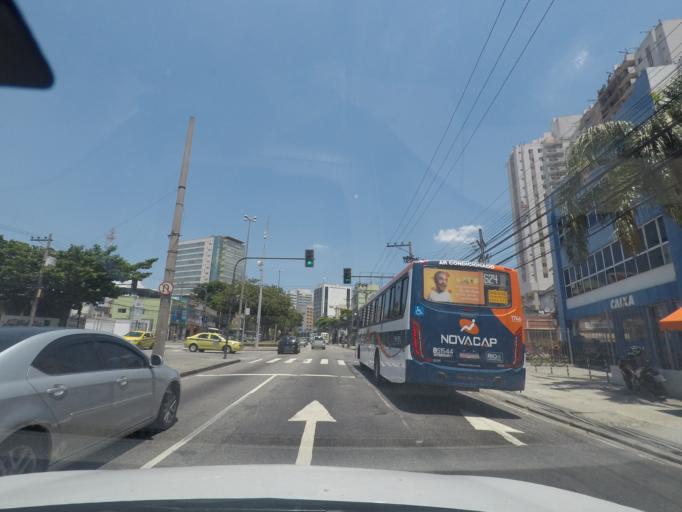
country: BR
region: Rio de Janeiro
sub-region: Rio De Janeiro
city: Rio de Janeiro
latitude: -22.8870
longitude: -43.2875
